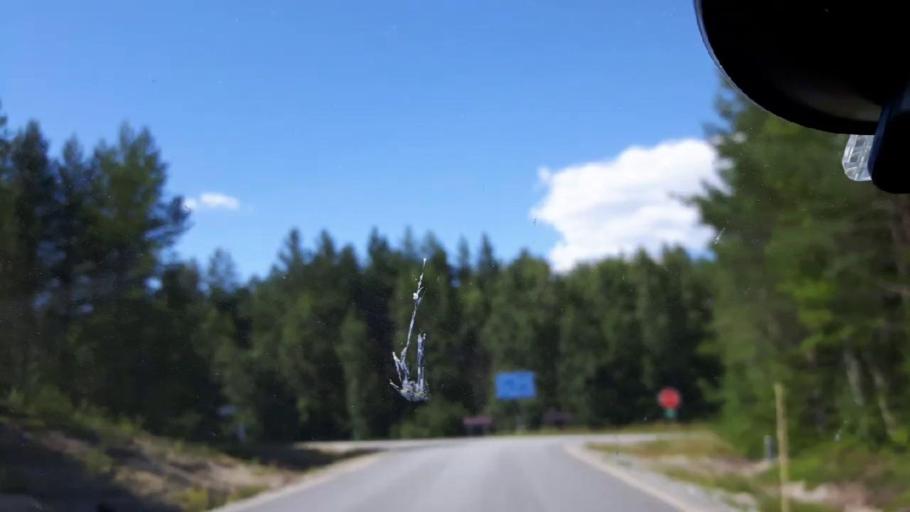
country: SE
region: Vaesternorrland
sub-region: Ange Kommun
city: Fransta
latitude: 62.7027
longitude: 16.3786
